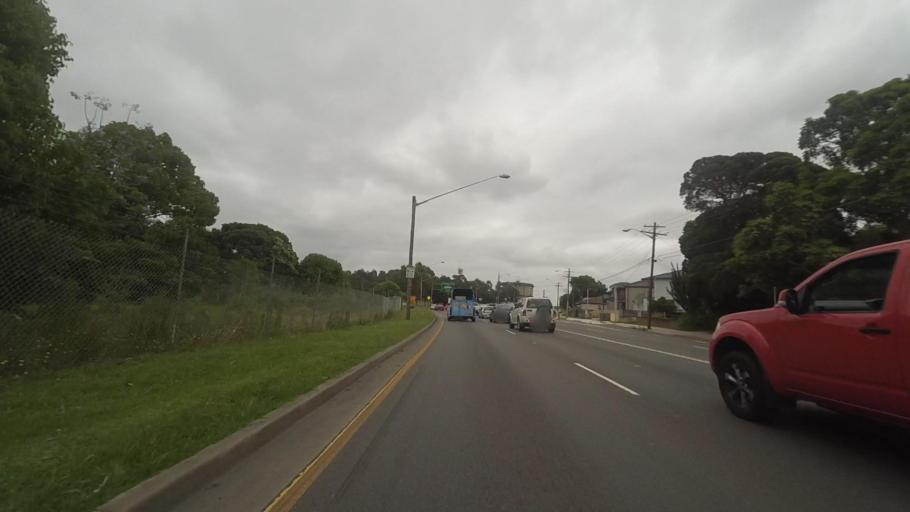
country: AU
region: New South Wales
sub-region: Bankstown
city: Bankstown
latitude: -33.9083
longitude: 151.0410
